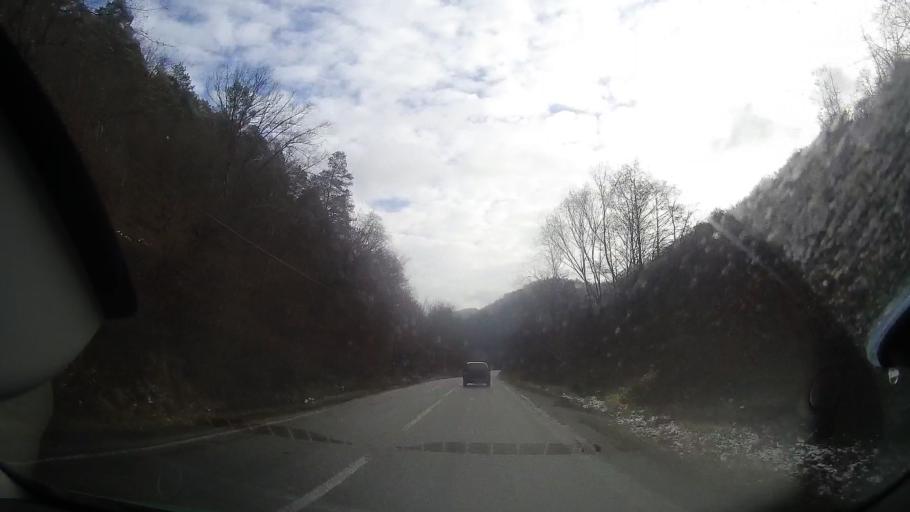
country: RO
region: Alba
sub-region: Oras Baia de Aries
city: Baia de Aries
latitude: 46.3824
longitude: 23.2620
